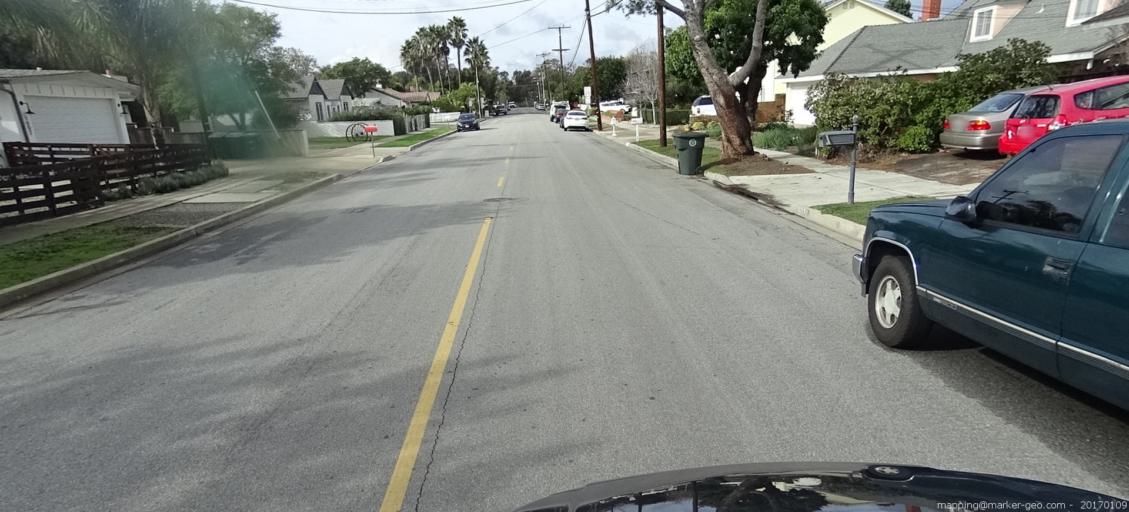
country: US
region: California
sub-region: Orange County
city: Costa Mesa
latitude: 33.6618
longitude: -117.8821
